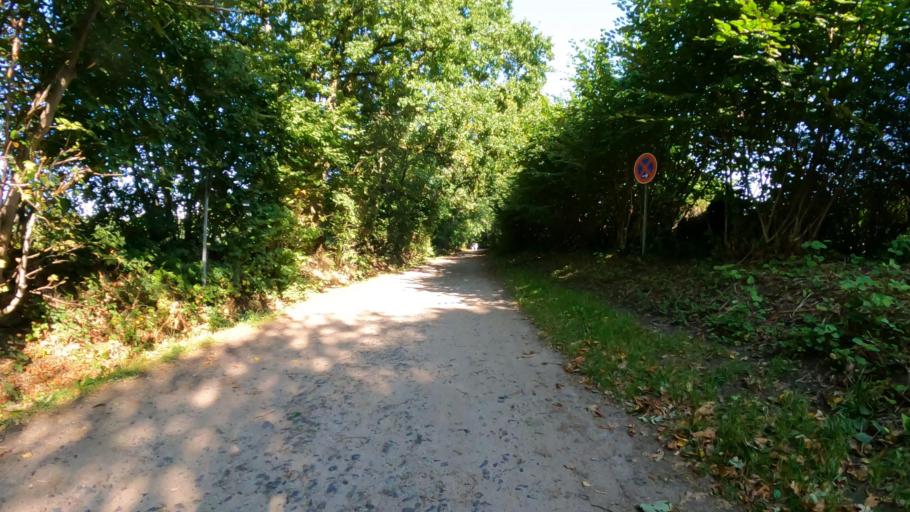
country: DE
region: Schleswig-Holstein
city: Ahrensburg
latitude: 53.6660
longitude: 10.2014
